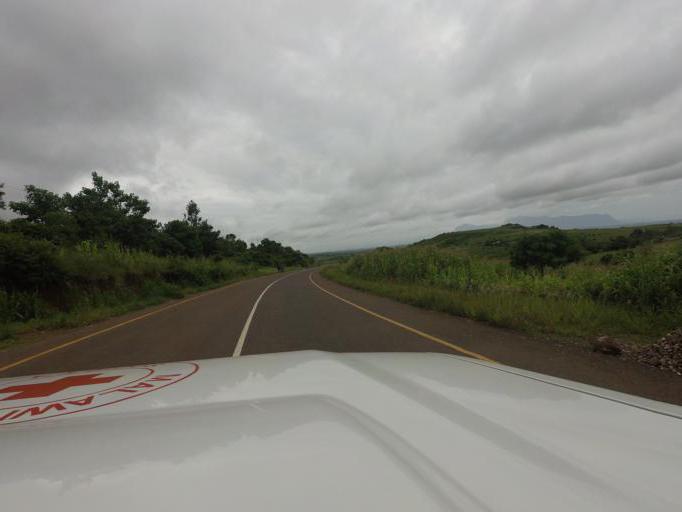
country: MW
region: Southern Region
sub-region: Thyolo District
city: Thyolo
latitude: -15.9638
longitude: 35.1860
